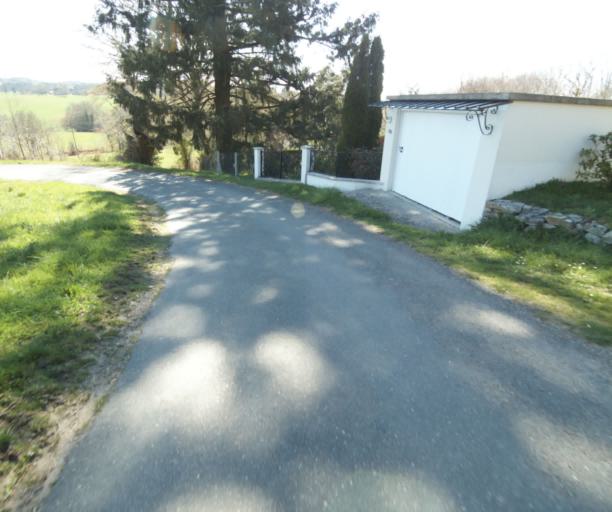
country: FR
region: Limousin
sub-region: Departement de la Correze
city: Saint-Mexant
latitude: 45.2885
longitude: 1.6990
